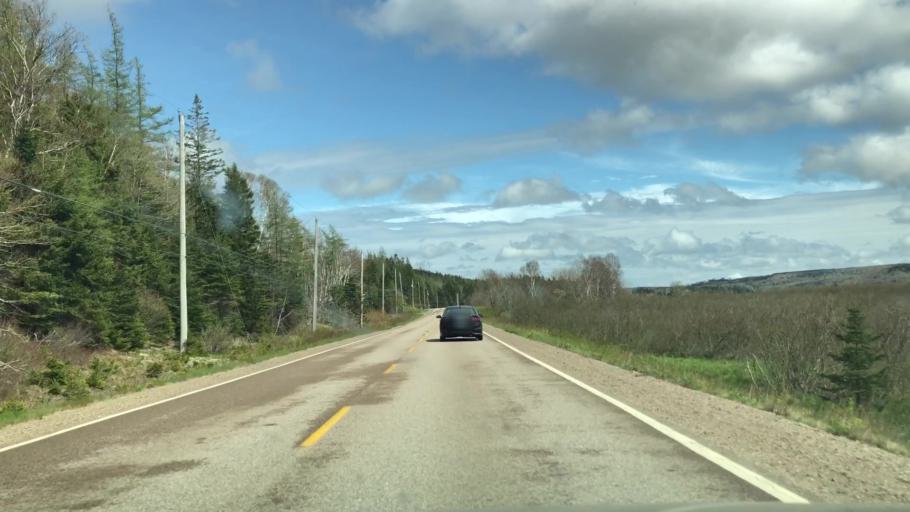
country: CA
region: Nova Scotia
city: Antigonish
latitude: 45.1932
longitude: -61.9956
